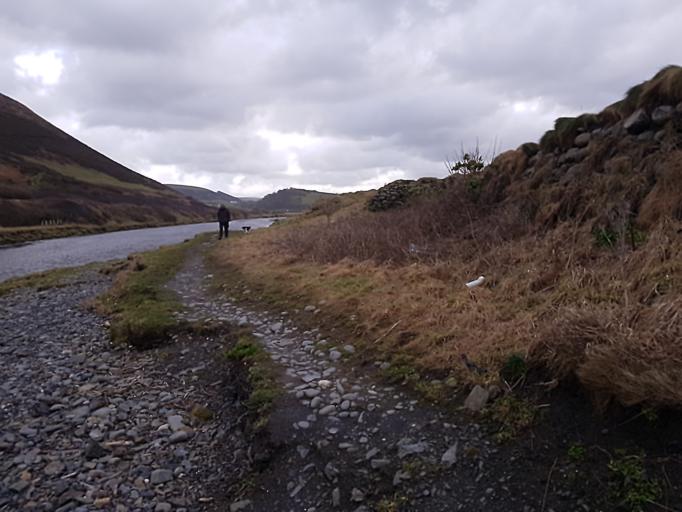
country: GB
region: Wales
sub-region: County of Ceredigion
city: Aberystwyth
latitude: 52.4051
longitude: -4.0893
